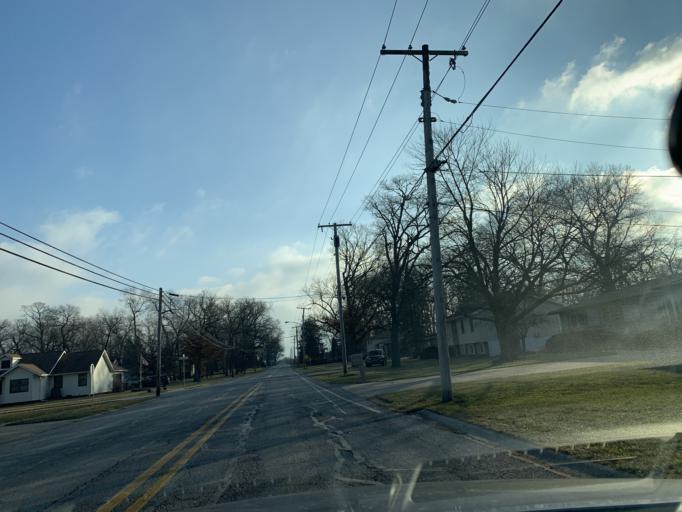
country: US
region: Indiana
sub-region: Porter County
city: Portage
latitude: 41.5868
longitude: -87.1566
